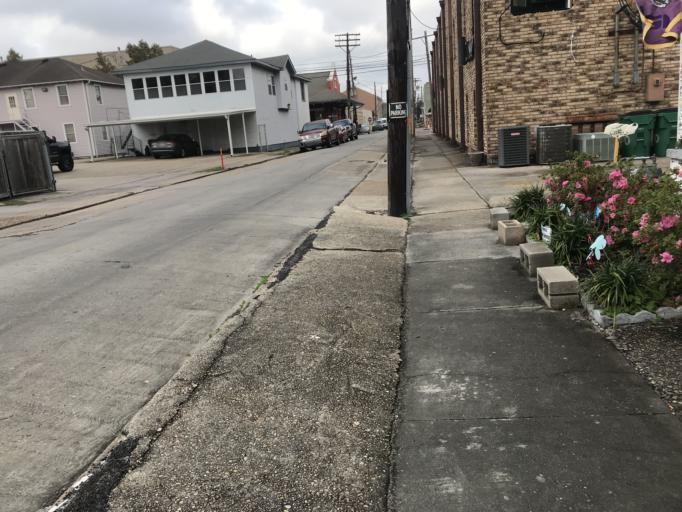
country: US
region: Louisiana
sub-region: Jefferson Parish
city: Gretna
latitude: 29.9159
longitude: -90.0659
